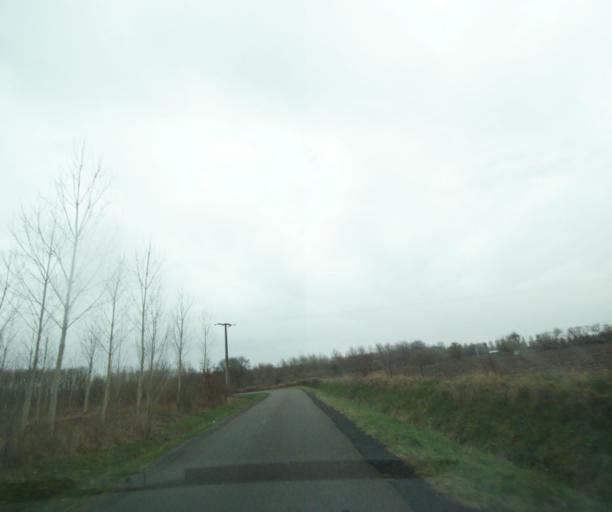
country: FR
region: Nord-Pas-de-Calais
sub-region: Departement du Nord
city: Vicq
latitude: 50.4208
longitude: 3.6262
